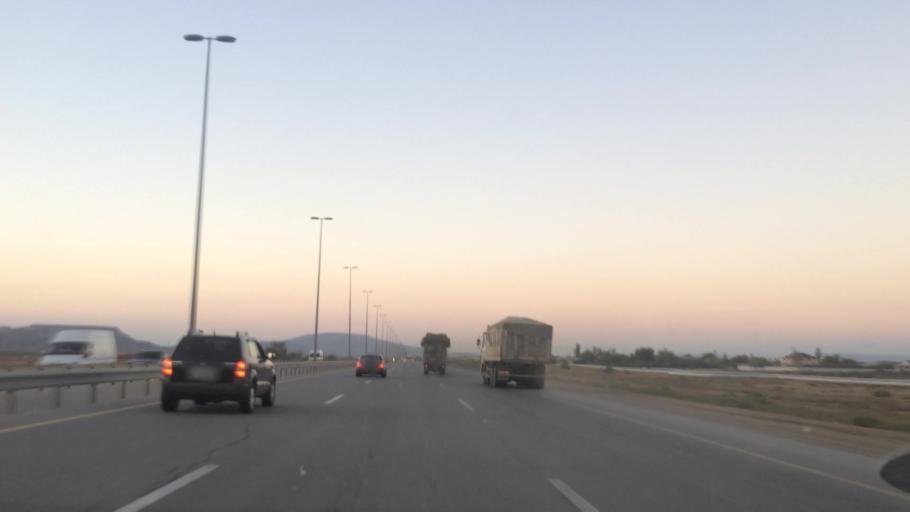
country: AZ
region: Baki
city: Qobustan
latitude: 40.0180
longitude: 49.4256
